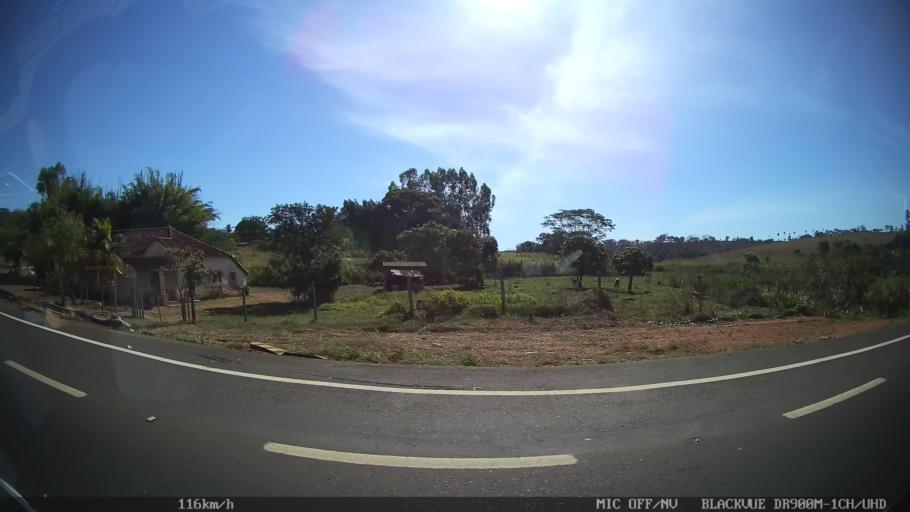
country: BR
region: Sao Paulo
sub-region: Olimpia
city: Olimpia
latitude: -20.6156
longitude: -48.7597
